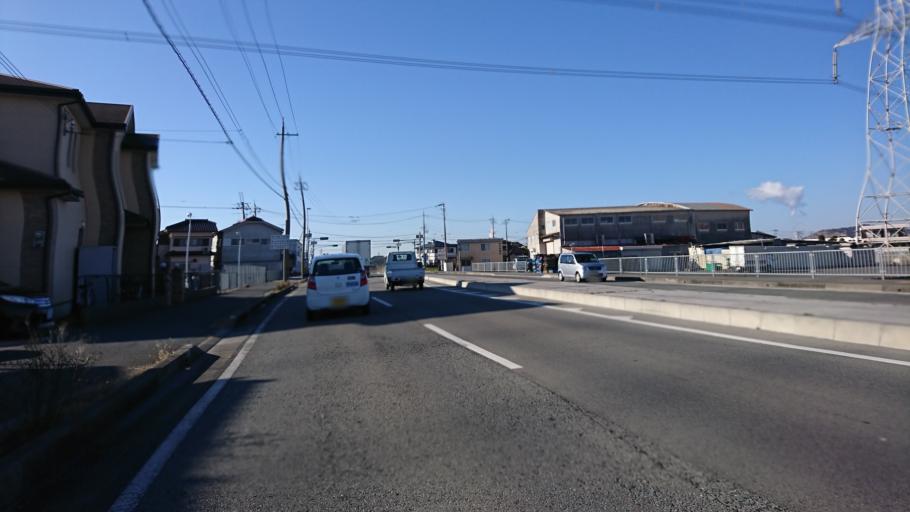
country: JP
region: Hyogo
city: Kakogawacho-honmachi
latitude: 34.7984
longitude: 134.8286
